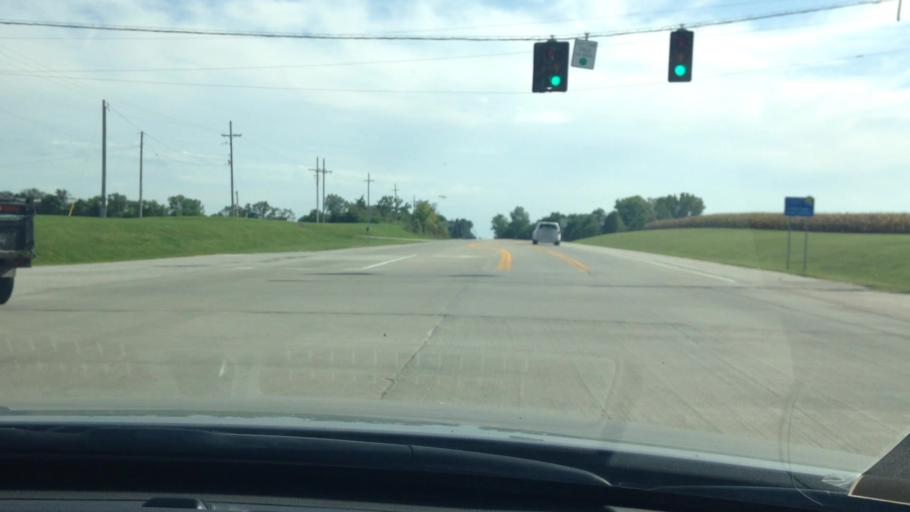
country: US
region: Missouri
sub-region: Cass County
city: Belton
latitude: 38.8180
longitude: -94.5858
